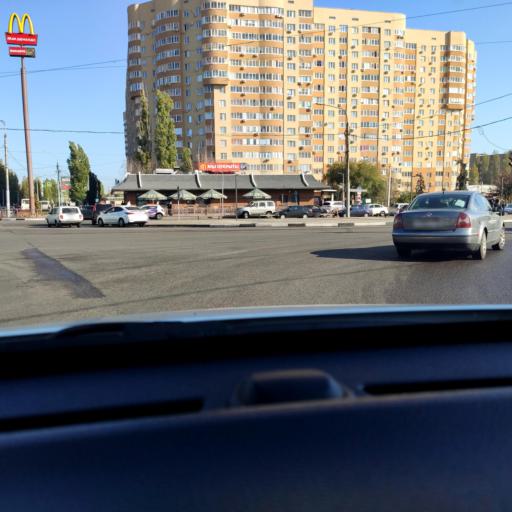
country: RU
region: Voronezj
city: Voronezh
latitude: 51.6724
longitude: 39.2528
